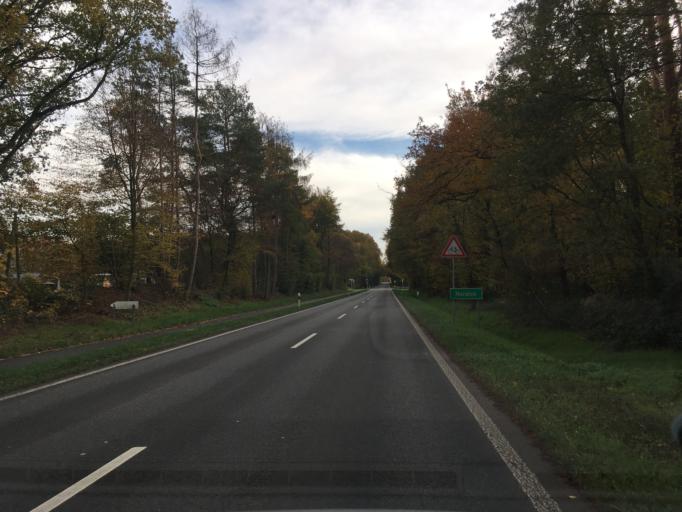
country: DE
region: North Rhine-Westphalia
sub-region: Regierungsbezirk Munster
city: Heiden
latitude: 51.8474
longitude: 6.9252
